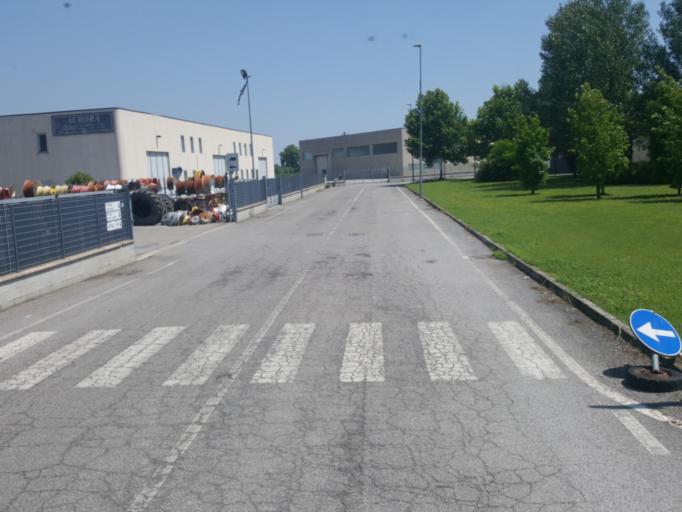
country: IT
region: Lombardy
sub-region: Provincia di Cremona
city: Calvatone
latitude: 45.1152
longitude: 10.4550
